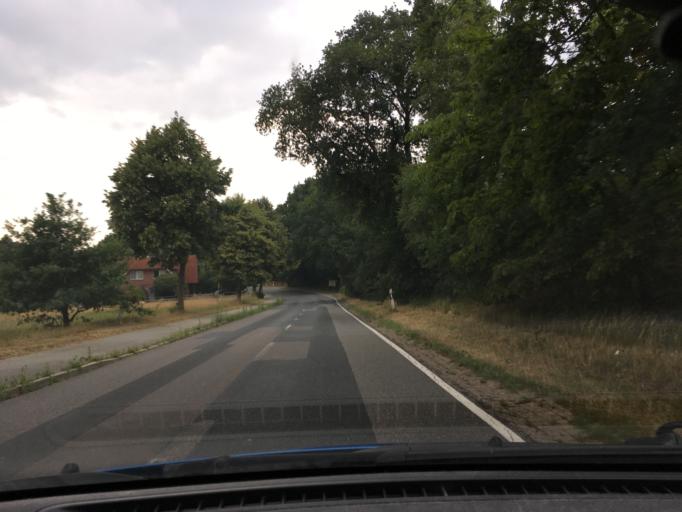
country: DE
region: Lower Saxony
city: Drestedt
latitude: 53.3259
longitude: 9.7766
